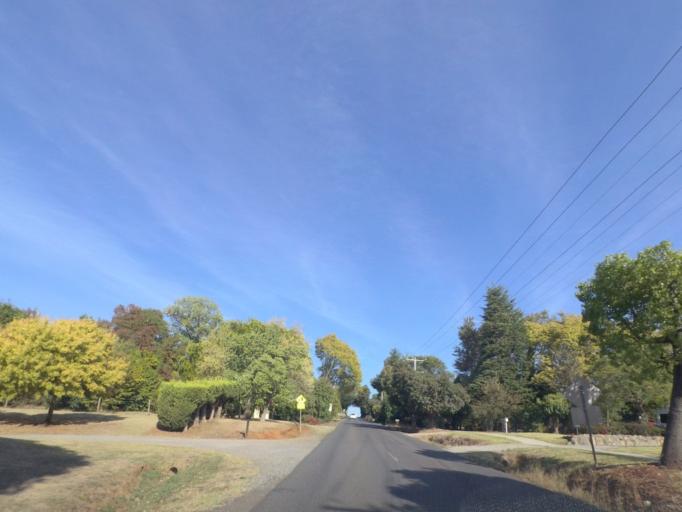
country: AU
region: Victoria
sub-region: Yarra Ranges
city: Mount Evelyn
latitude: -37.7888
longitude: 145.4337
